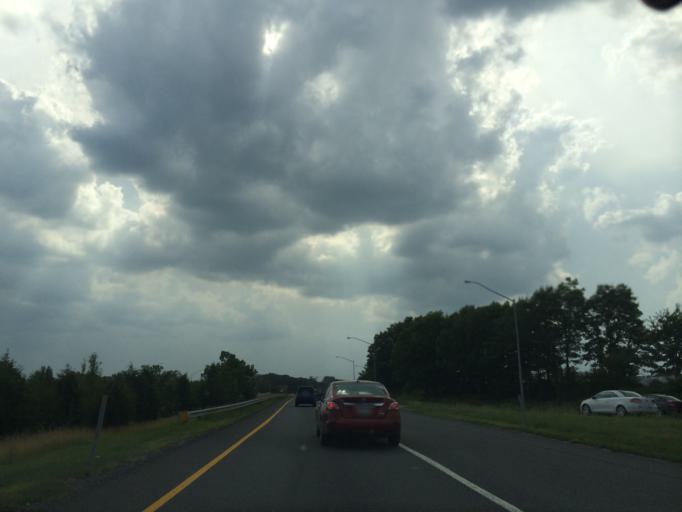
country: US
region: Maryland
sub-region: Baltimore County
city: Woodlawn
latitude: 39.3067
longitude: -76.7480
